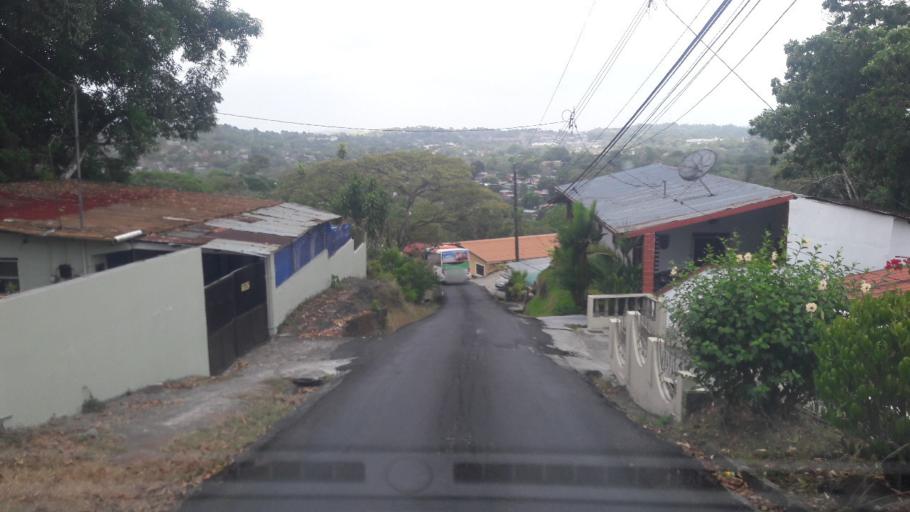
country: PA
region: Panama
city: Alcalde Diaz
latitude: 9.1250
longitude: -79.5527
